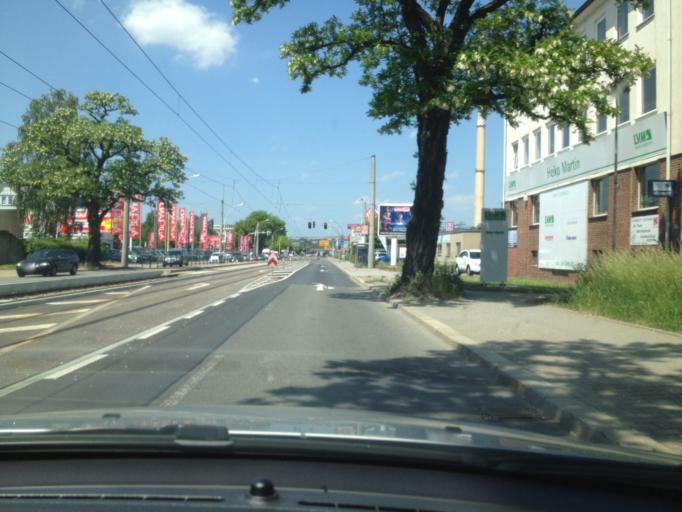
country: DE
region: Saxony
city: Chemnitz
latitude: 50.7938
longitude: 12.9231
